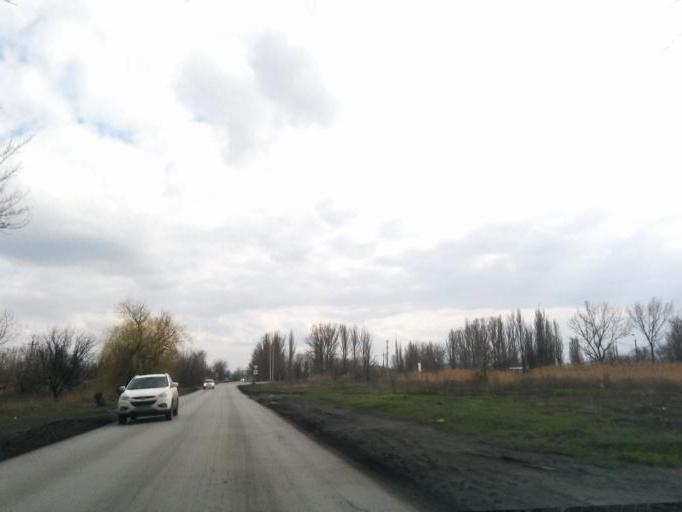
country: RU
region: Rostov
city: Shakhty
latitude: 47.6803
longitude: 40.2846
